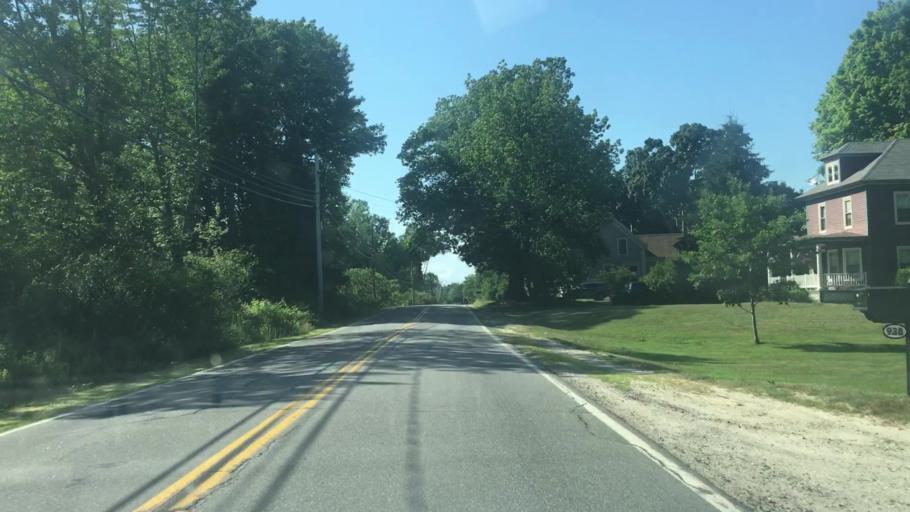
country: US
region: Maine
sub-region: York County
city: Buxton
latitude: 43.6227
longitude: -70.5467
